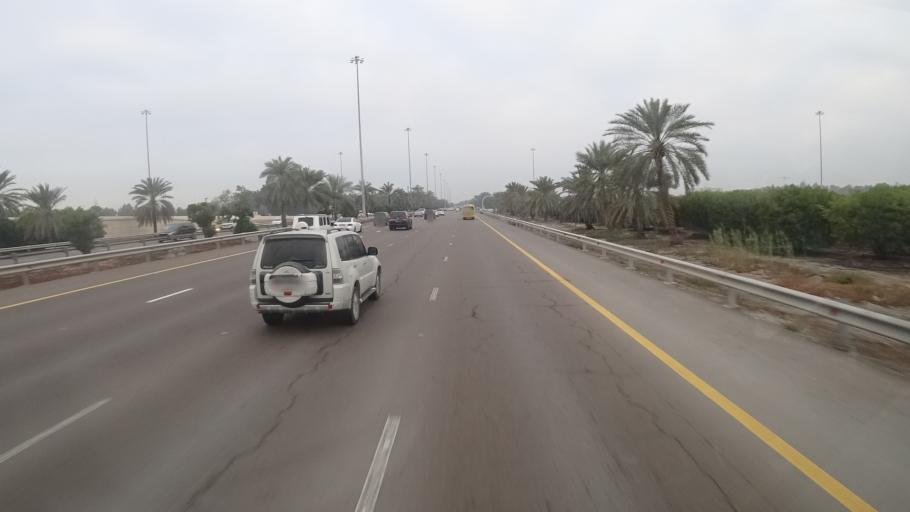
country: AE
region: Abu Dhabi
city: Abu Dhabi
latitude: 24.3532
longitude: 54.5689
